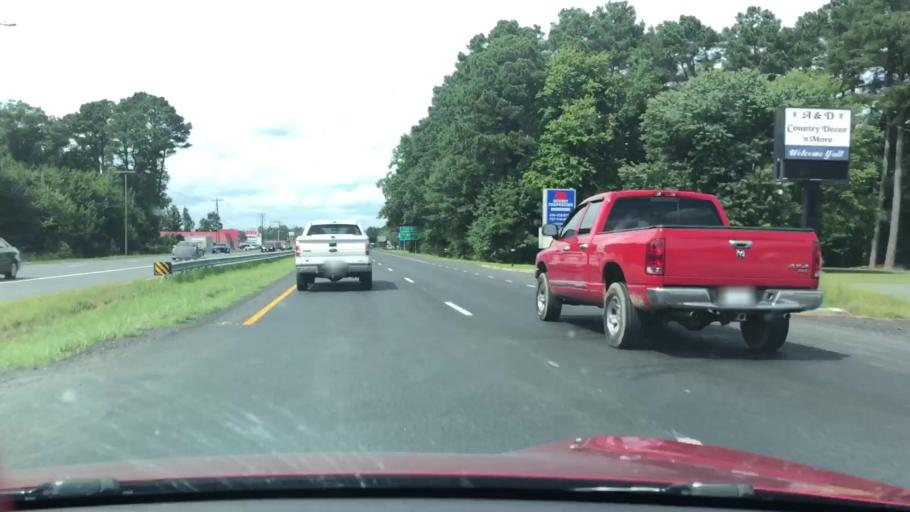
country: US
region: Maryland
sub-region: Worcester County
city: Pocomoke City
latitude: 38.0406
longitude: -75.5423
